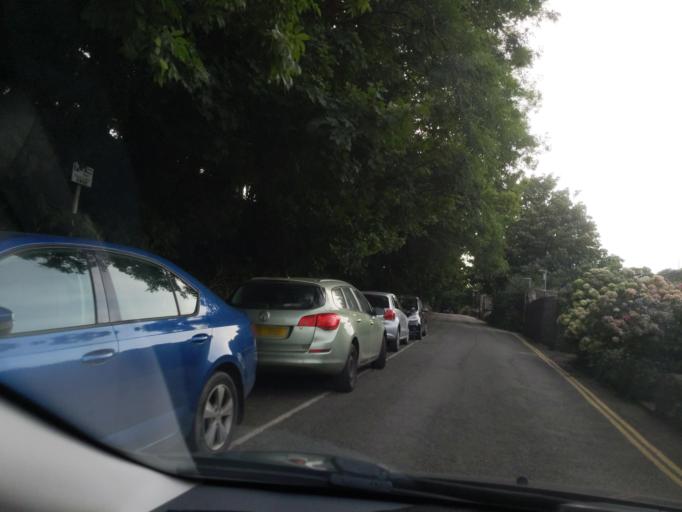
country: GB
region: England
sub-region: Cornwall
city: Millbrook
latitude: 50.3312
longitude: -4.2037
